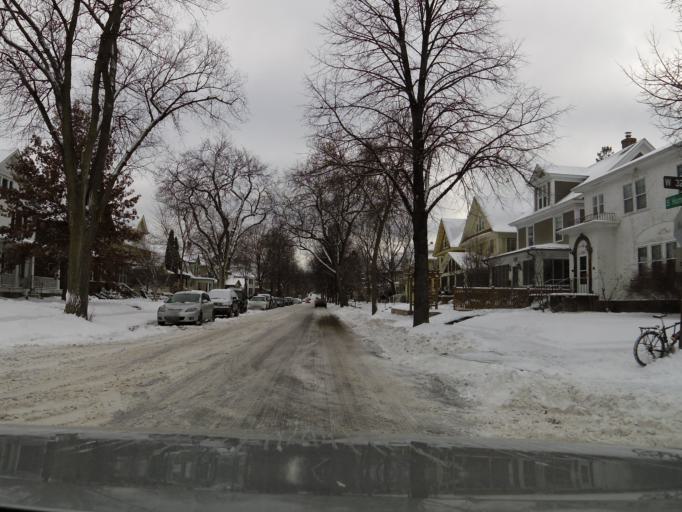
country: US
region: Minnesota
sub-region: Hennepin County
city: Saint Louis Park
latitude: 44.9447
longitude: -93.3009
